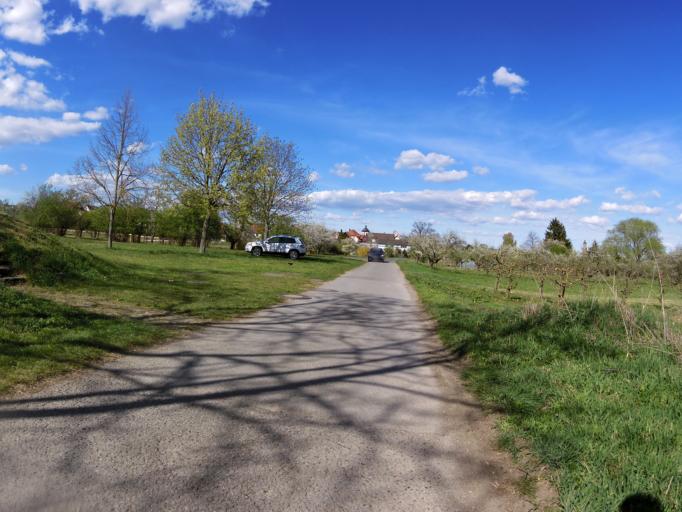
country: DE
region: Bavaria
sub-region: Regierungsbezirk Unterfranken
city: Volkach
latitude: 49.8590
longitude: 10.2161
